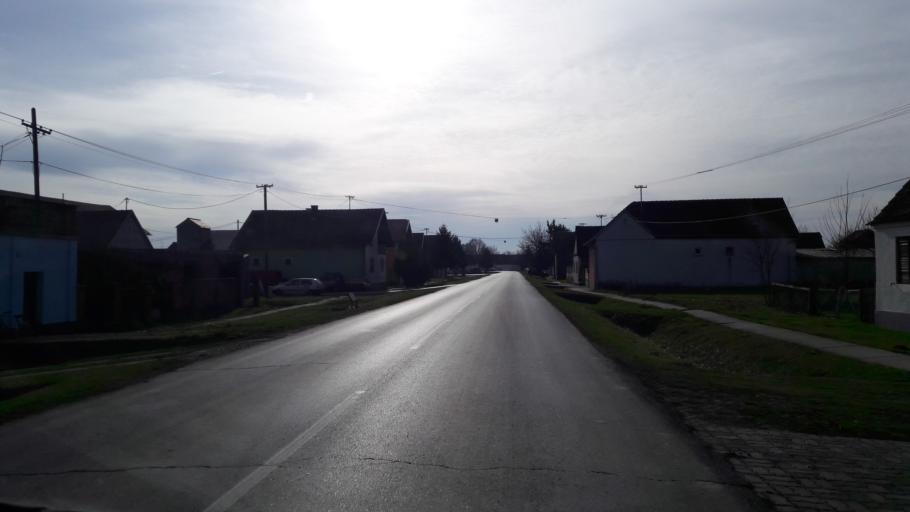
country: HR
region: Osjecko-Baranjska
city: Semeljci
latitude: 45.3113
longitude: 18.5572
